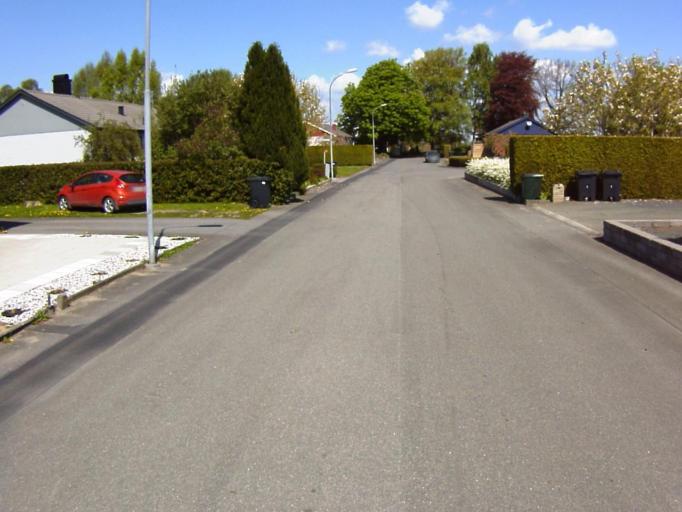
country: SE
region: Skane
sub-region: Kristianstads Kommun
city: Fjalkinge
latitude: 56.0144
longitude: 14.2270
